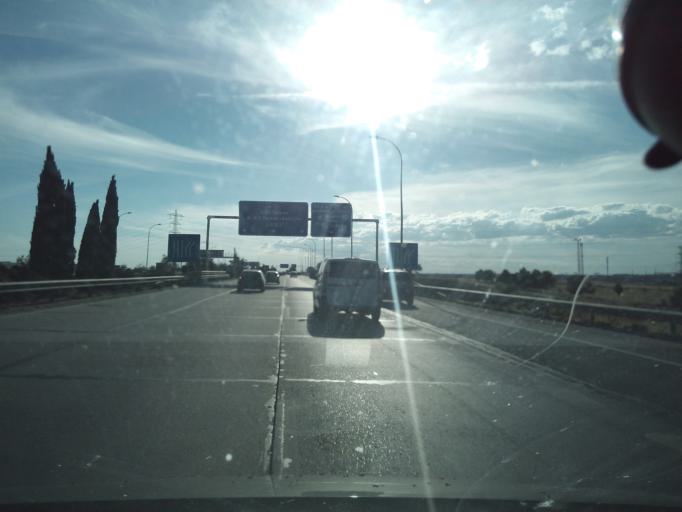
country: ES
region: Madrid
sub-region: Provincia de Madrid
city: Pinto
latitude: 40.2732
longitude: -3.7056
